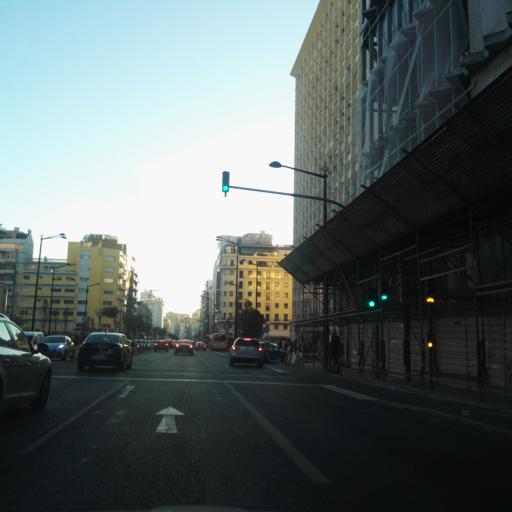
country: PT
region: Lisbon
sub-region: Lisbon
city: Lisbon
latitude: 38.7320
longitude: -9.1460
